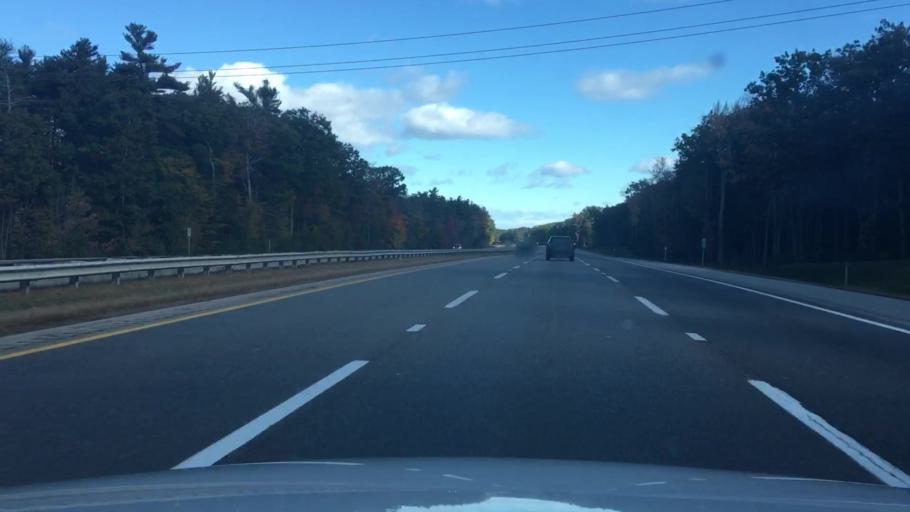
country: US
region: Maine
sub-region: York County
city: Ogunquit
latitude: 43.2502
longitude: -70.6240
